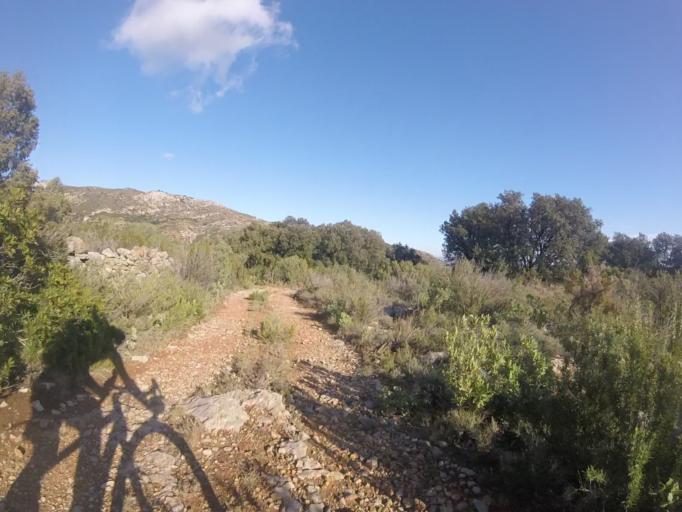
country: ES
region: Valencia
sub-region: Provincia de Castello
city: Sarratella
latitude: 40.2955
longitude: 0.0488
